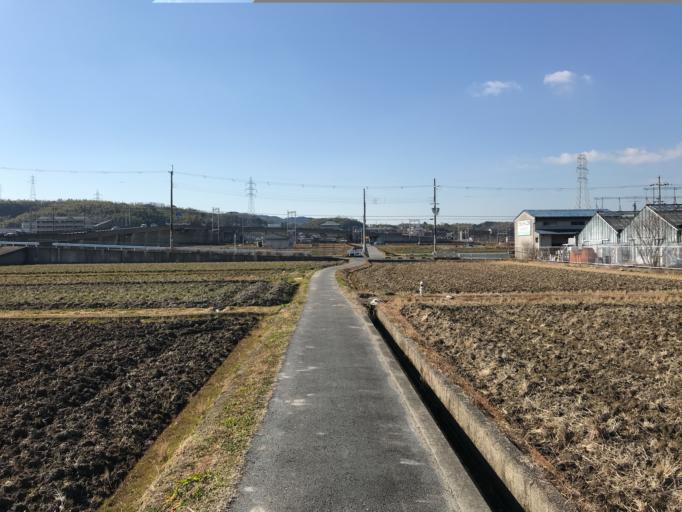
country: JP
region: Kyoto
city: Tanabe
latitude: 34.8148
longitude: 135.7773
